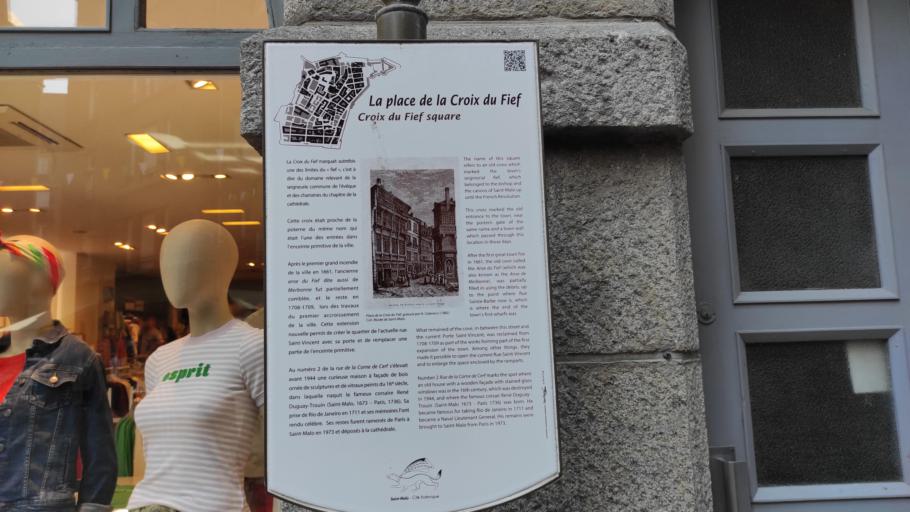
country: FR
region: Brittany
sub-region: Departement d'Ille-et-Vilaine
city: Saint-Malo
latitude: 48.6501
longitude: -2.0249
